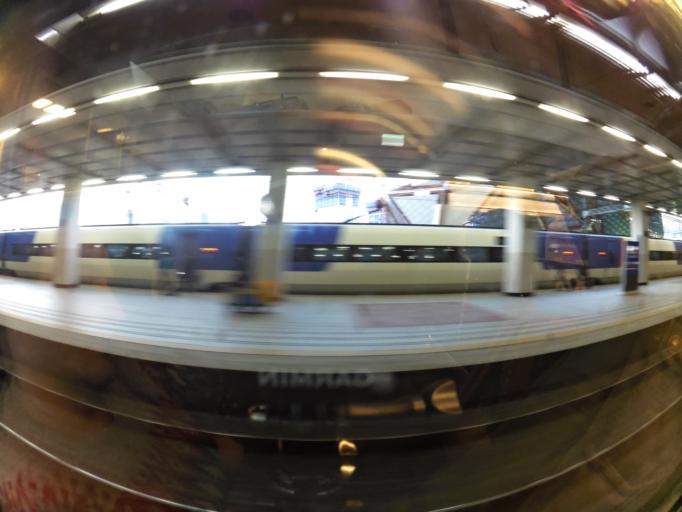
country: KR
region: Seoul
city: Seoul
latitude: 37.5296
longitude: 126.9635
